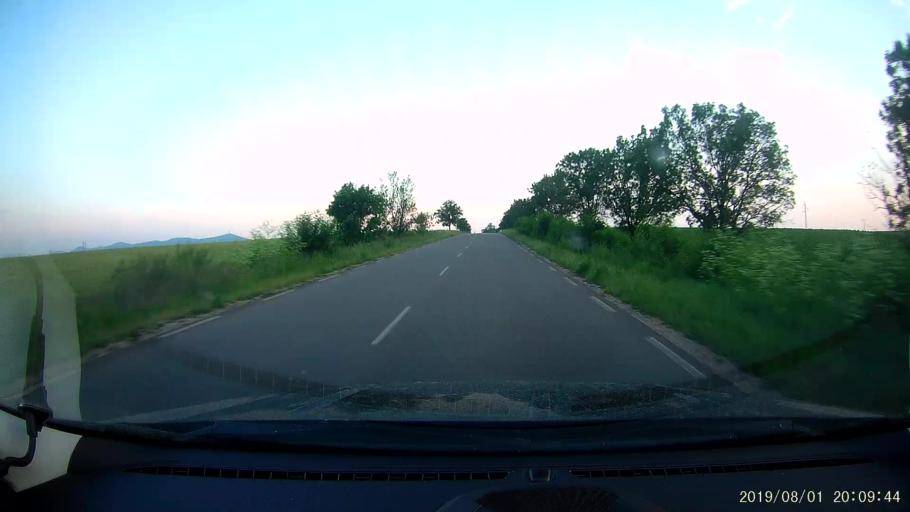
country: BG
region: Yambol
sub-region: Obshtina Yambol
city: Yambol
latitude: 42.4937
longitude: 26.5939
